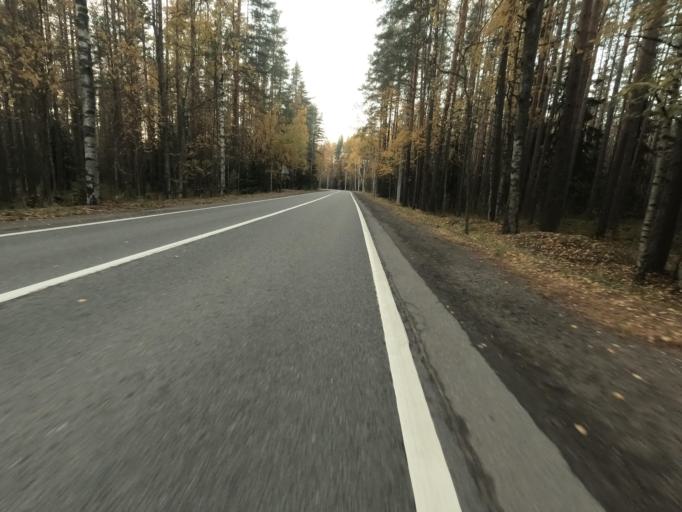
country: RU
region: St.-Petersburg
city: Repino
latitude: 60.1895
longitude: 29.8630
